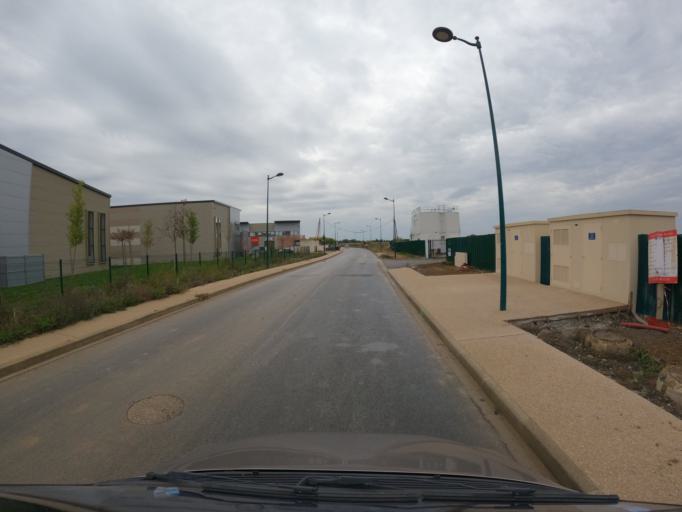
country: FR
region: Ile-de-France
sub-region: Departement de Seine-et-Marne
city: Serris
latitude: 48.8425
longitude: 2.7996
